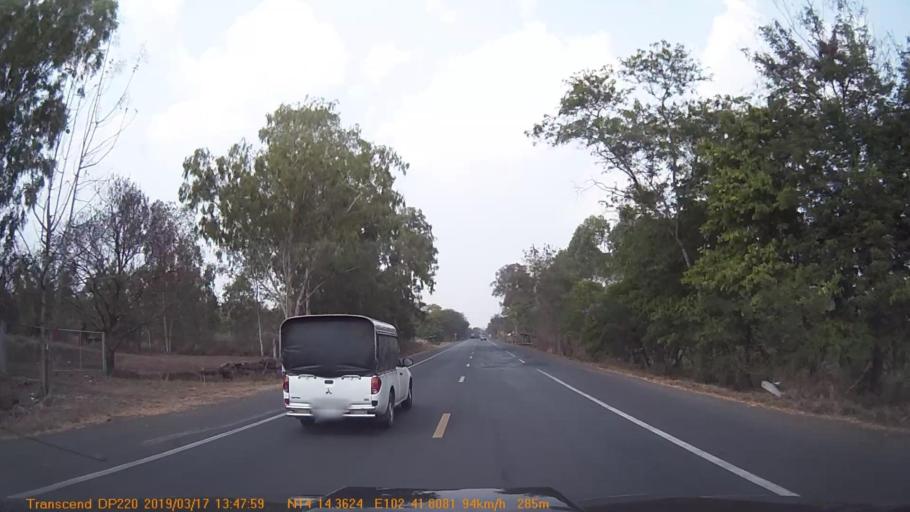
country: TH
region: Buriram
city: Non Din Daeng
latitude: 14.2398
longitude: 102.6969
